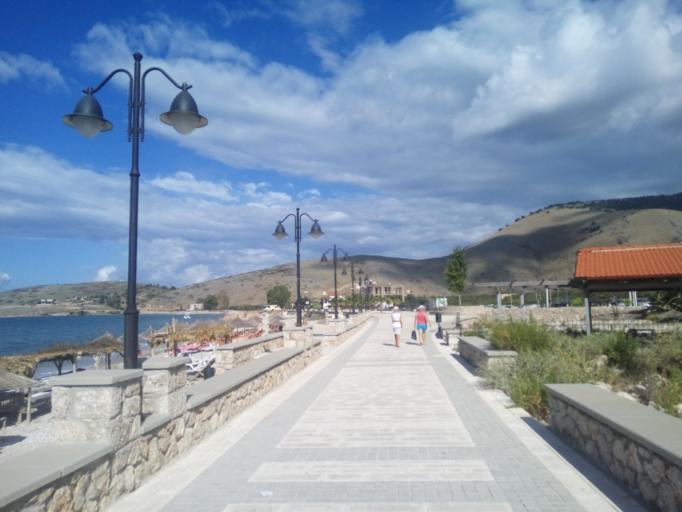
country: AL
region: Vlore
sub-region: Rrethi i Vlores
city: Himare
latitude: 40.0527
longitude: 19.8266
